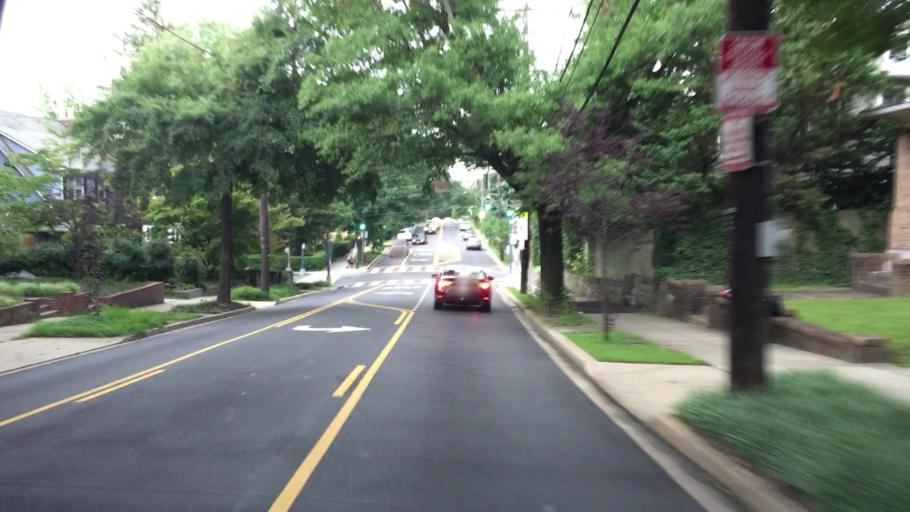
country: US
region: Maryland
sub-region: Montgomery County
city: Friendship Village
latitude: 38.9321
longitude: -77.0664
